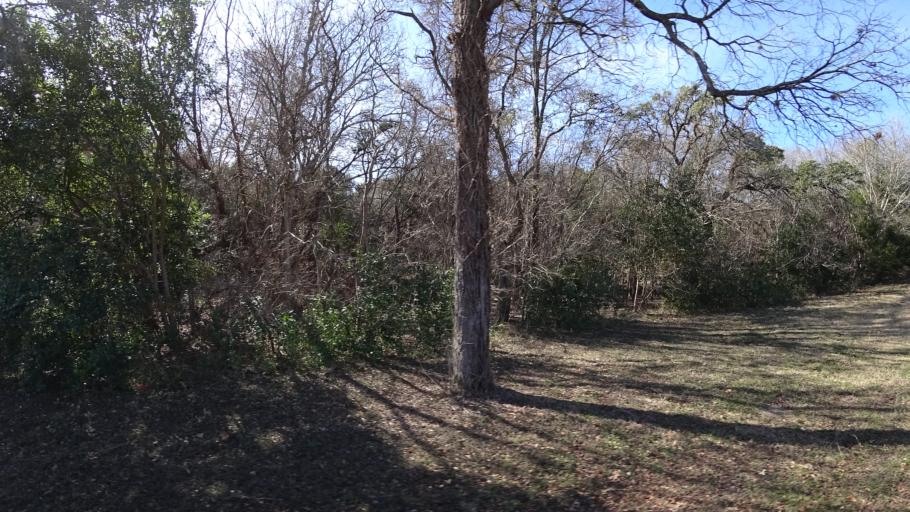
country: US
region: Texas
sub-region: Travis County
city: Wells Branch
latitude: 30.3916
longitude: -97.6843
